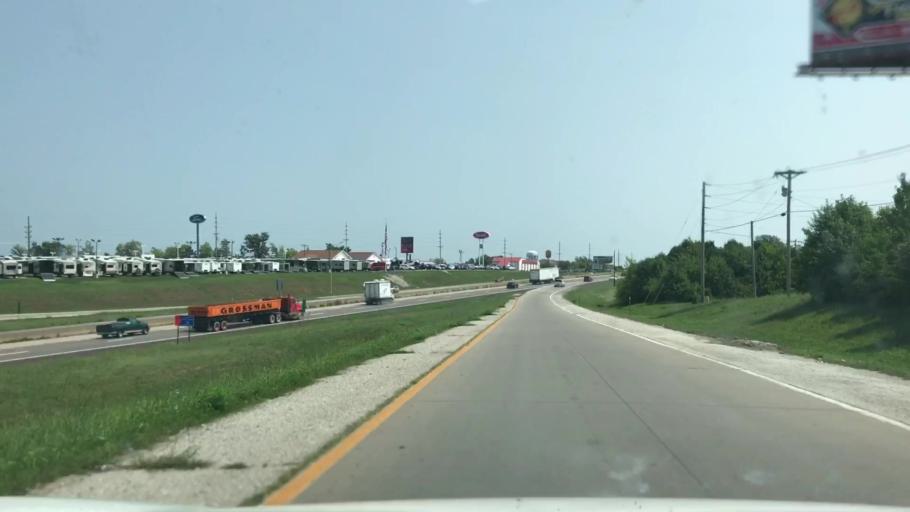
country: US
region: Missouri
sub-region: Saint Charles County
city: Dardenne Prairie
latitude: 38.8025
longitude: -90.7322
